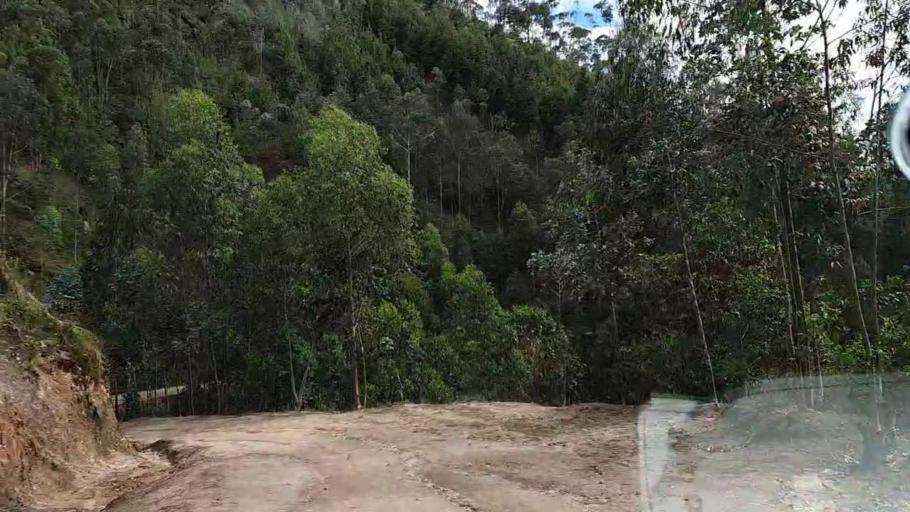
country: RW
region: Southern Province
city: Nzega
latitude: -2.4105
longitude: 29.4570
